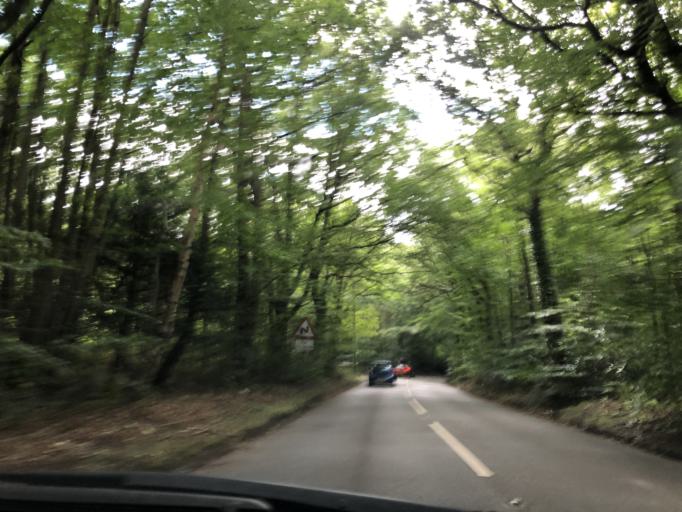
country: GB
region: England
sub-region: Kent
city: Westerham
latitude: 51.2547
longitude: 0.0795
